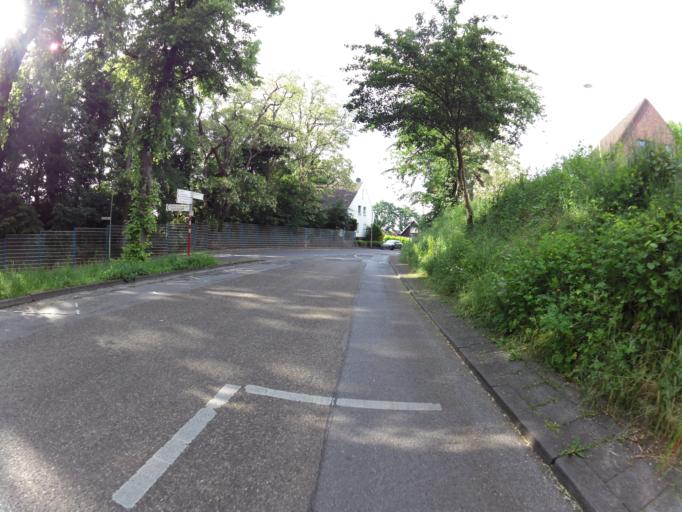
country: DE
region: North Rhine-Westphalia
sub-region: Regierungsbezirk Koln
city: Herzogenrath
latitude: 50.8736
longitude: 6.0976
